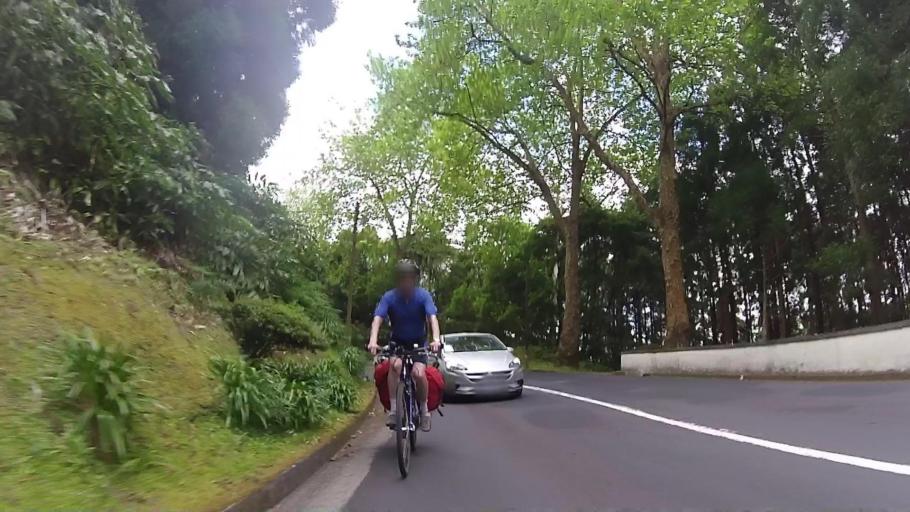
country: PT
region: Azores
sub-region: Povoacao
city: Furnas
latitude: 37.7630
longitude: -25.2863
